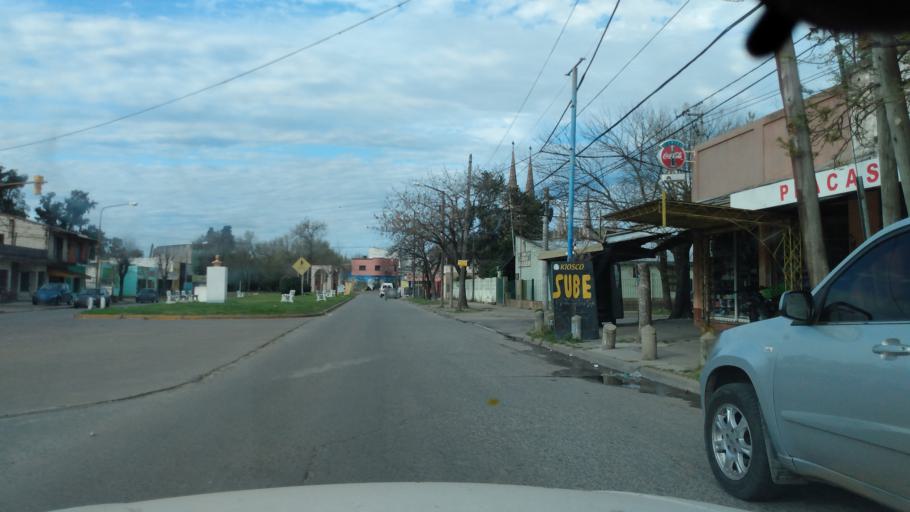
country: AR
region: Buenos Aires
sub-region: Partido de Lujan
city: Lujan
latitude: -34.5653
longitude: -59.1267
